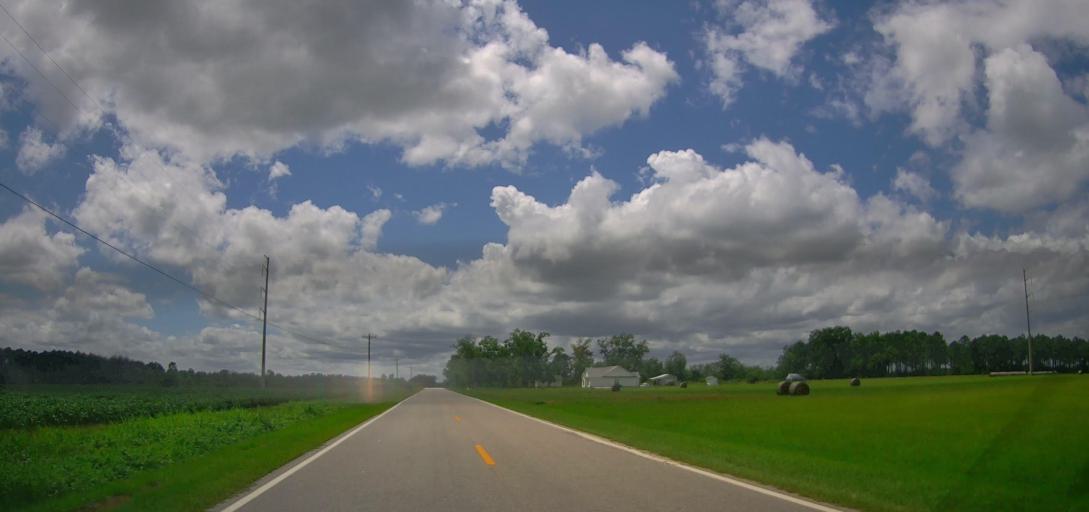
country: US
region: Georgia
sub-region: Irwin County
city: Ocilla
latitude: 31.6444
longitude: -83.2533
